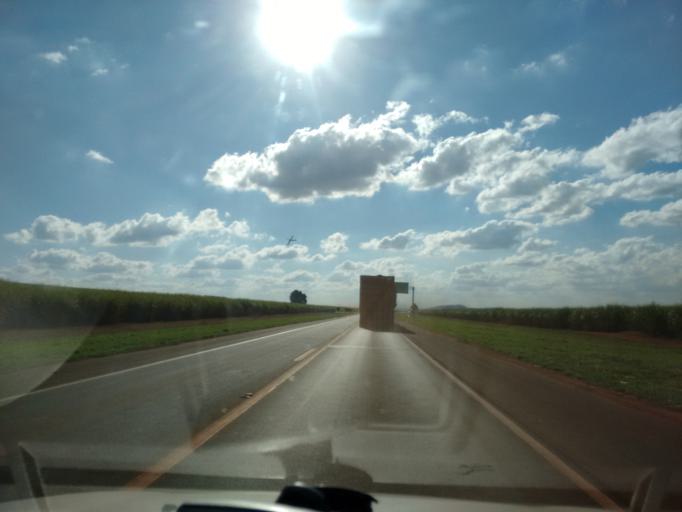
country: BR
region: Sao Paulo
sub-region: Americo Brasiliense
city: Americo Brasiliense
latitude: -21.6161
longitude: -48.0288
